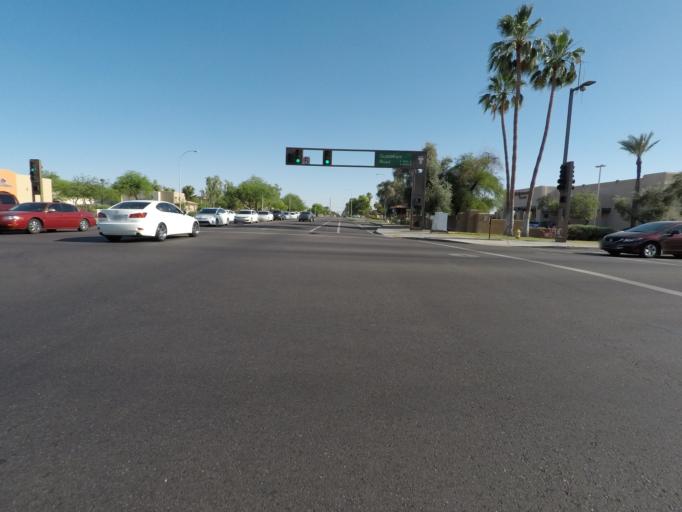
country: US
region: Arizona
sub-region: Maricopa County
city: Tempe
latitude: 33.3638
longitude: -111.9113
